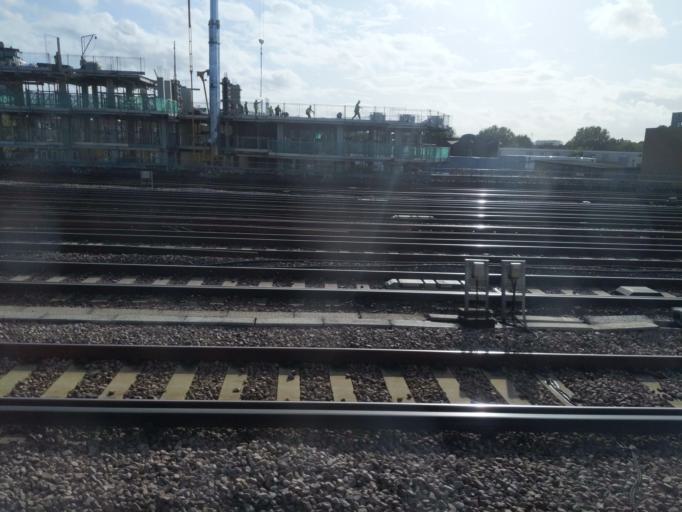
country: GB
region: England
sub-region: Greater London
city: Bethnal Green
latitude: 51.4930
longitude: -0.0616
